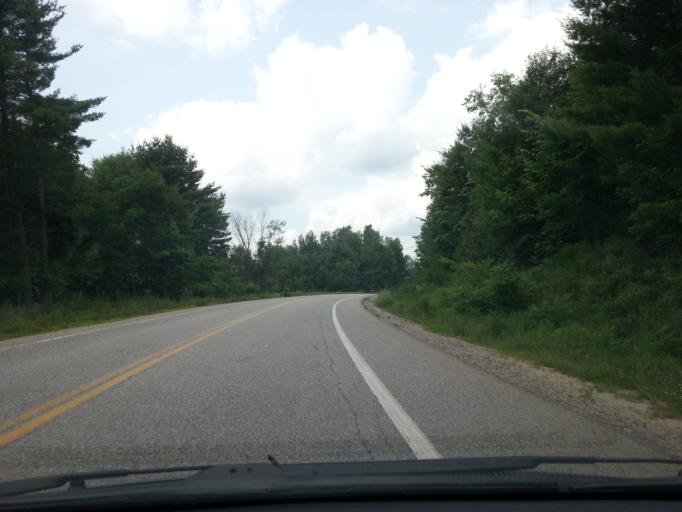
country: CA
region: Quebec
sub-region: Outaouais
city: Val-des-Monts
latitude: 45.6551
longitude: -75.6522
